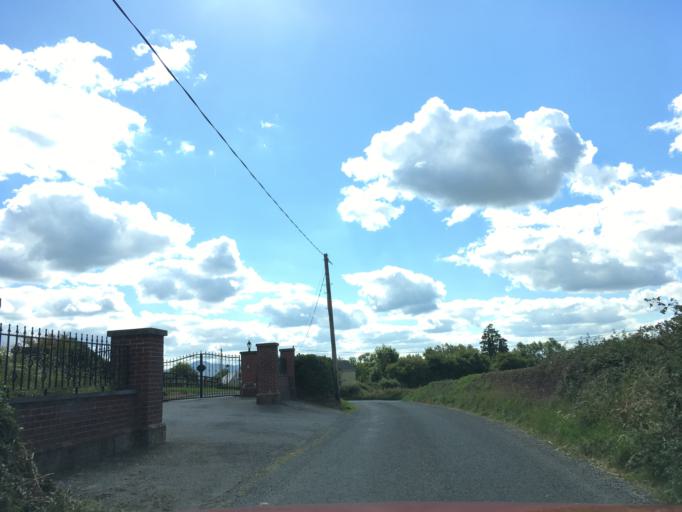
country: IE
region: Munster
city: Cashel
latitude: 52.4805
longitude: -7.9774
